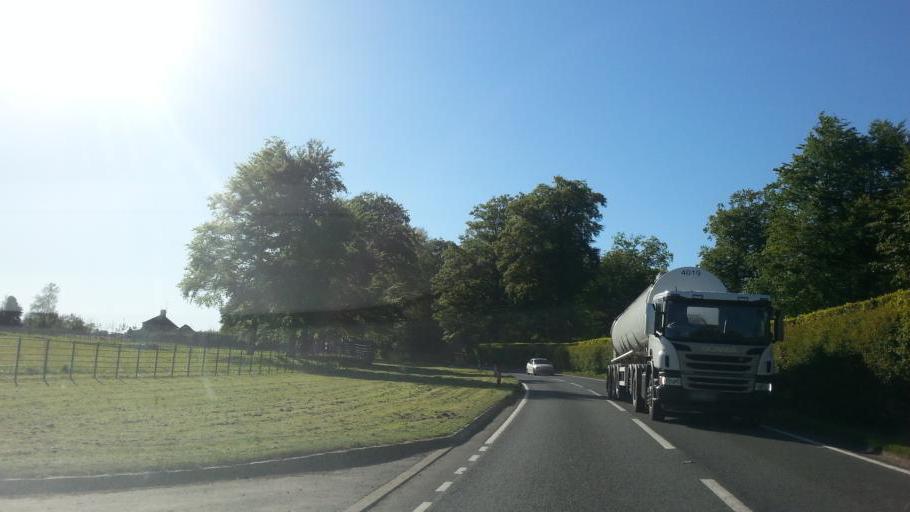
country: GB
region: England
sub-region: Somerset
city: Castle Cary
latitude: 51.0762
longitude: -2.4884
